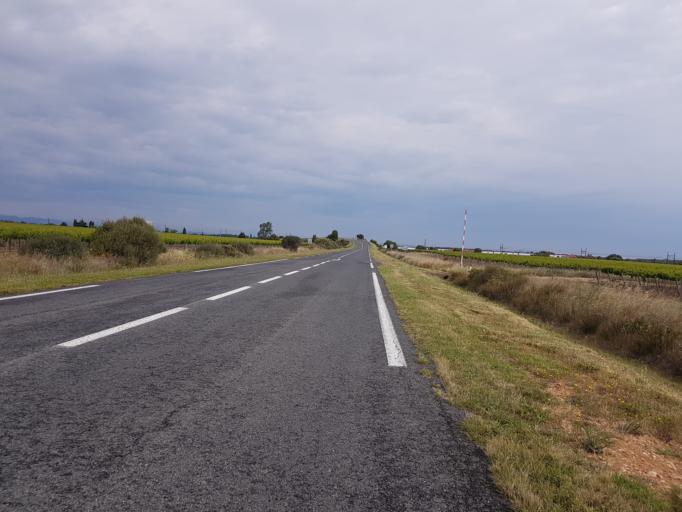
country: FR
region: Languedoc-Roussillon
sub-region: Departement de l'Herault
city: Portiragnes
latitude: 43.3161
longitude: 3.3604
